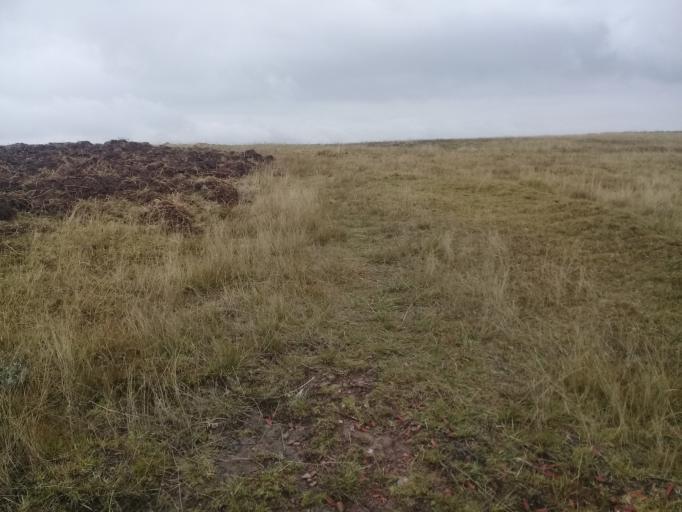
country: CO
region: Boyaca
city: Siachoque
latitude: 5.5654
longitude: -73.2740
